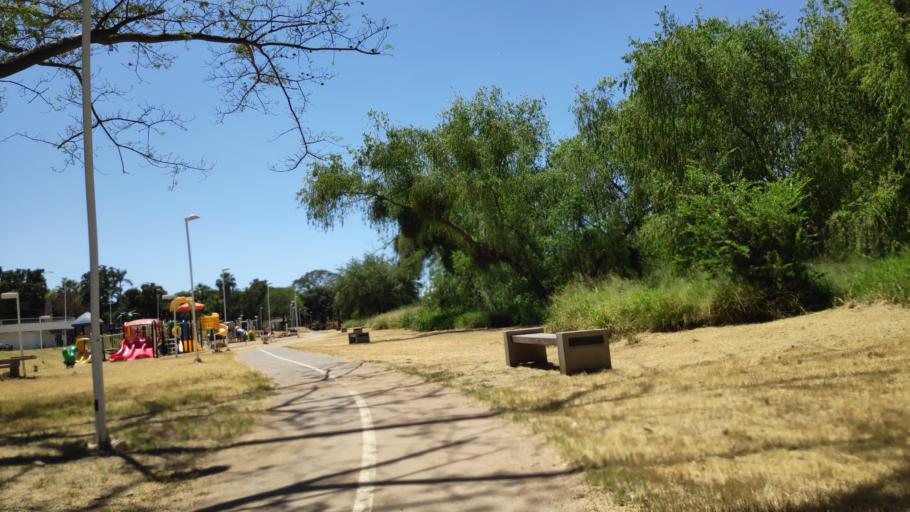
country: MX
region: Sinaloa
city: Culiacan
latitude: 24.8168
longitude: -107.3826
